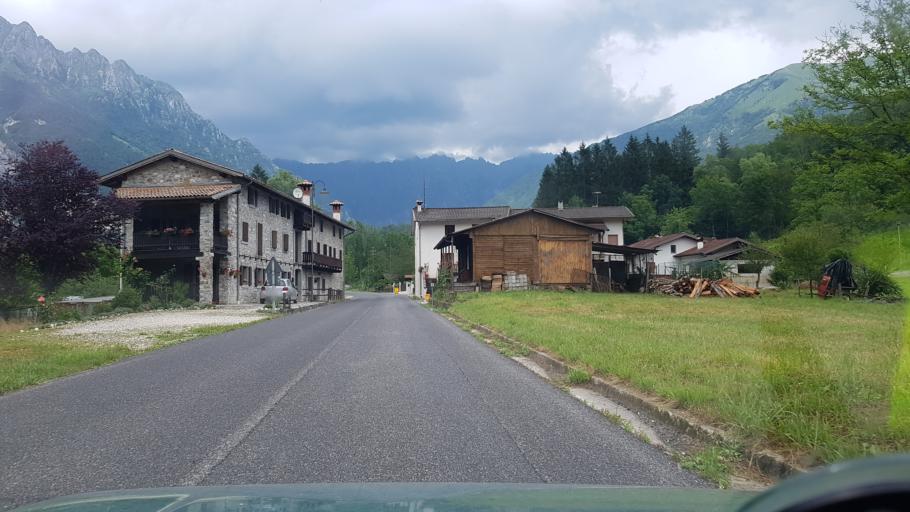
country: IT
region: Friuli Venezia Giulia
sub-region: Provincia di Udine
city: Lusevera
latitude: 46.2660
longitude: 13.2598
